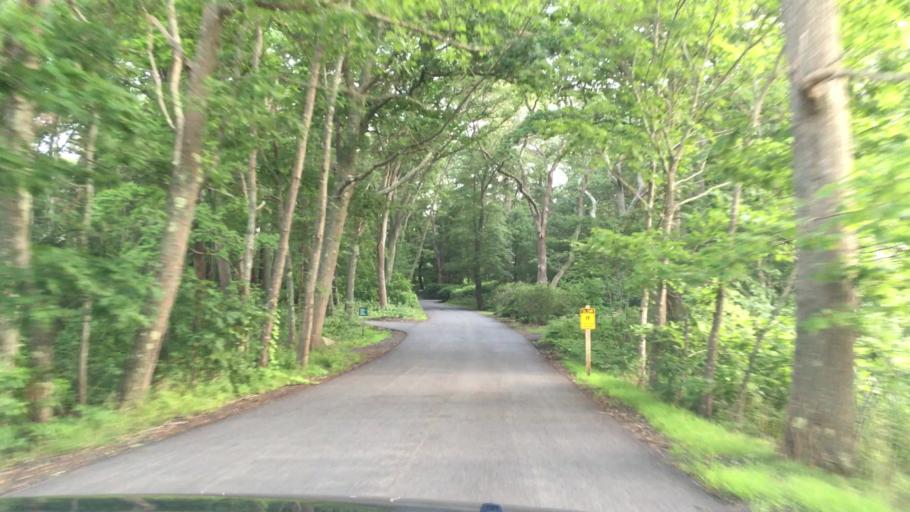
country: US
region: Massachusetts
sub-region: Essex County
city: Gloucester
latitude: 42.5764
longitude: -70.7259
